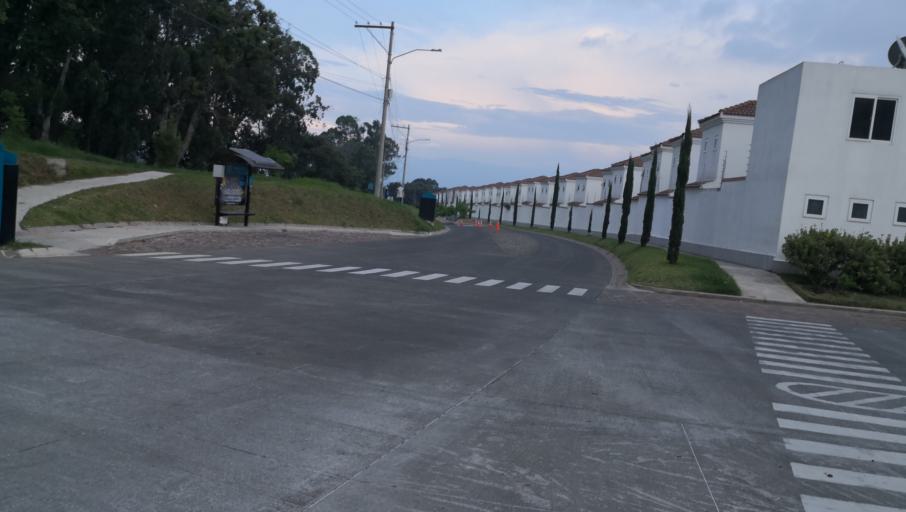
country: GT
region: Guatemala
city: Villa Nueva
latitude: 14.5627
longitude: -90.5982
